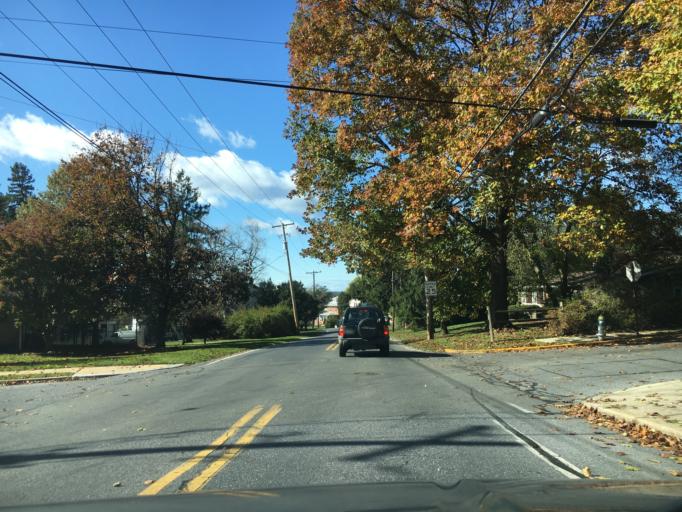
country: US
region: Pennsylvania
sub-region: Berks County
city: South Temple
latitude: 40.3911
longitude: -75.9062
